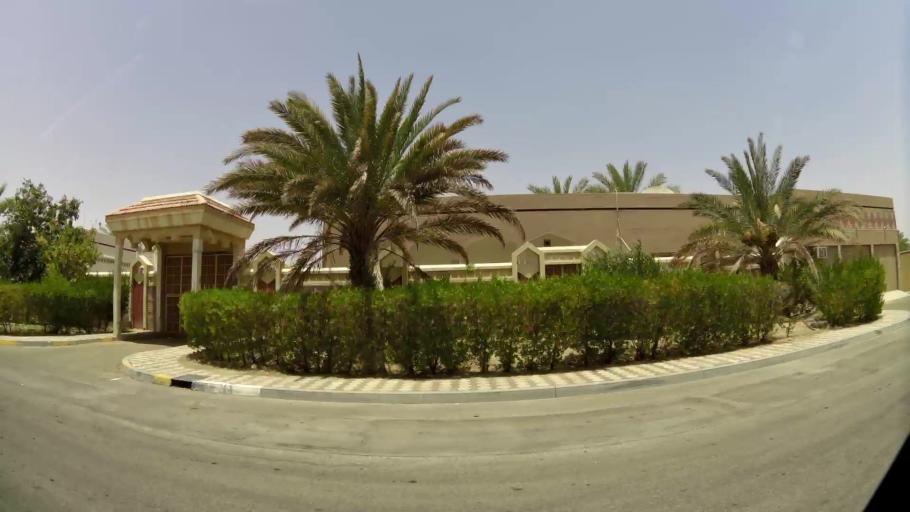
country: AE
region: Abu Dhabi
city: Al Ain
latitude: 24.2000
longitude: 55.7804
